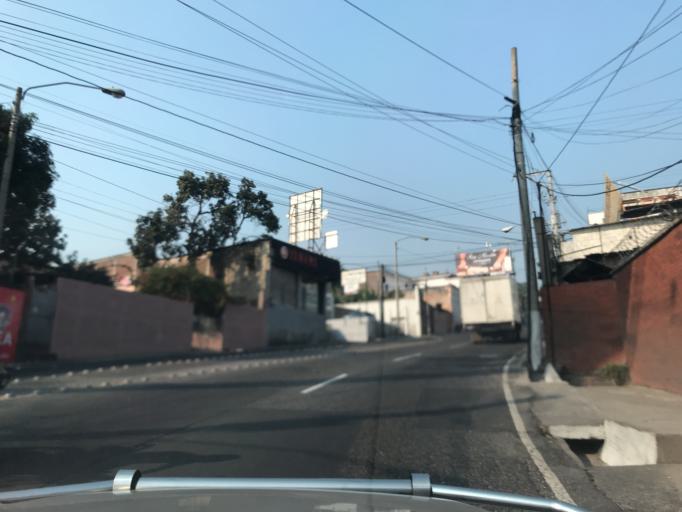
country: GT
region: Guatemala
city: Santa Catarina Pinula
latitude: 14.5641
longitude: -90.5287
